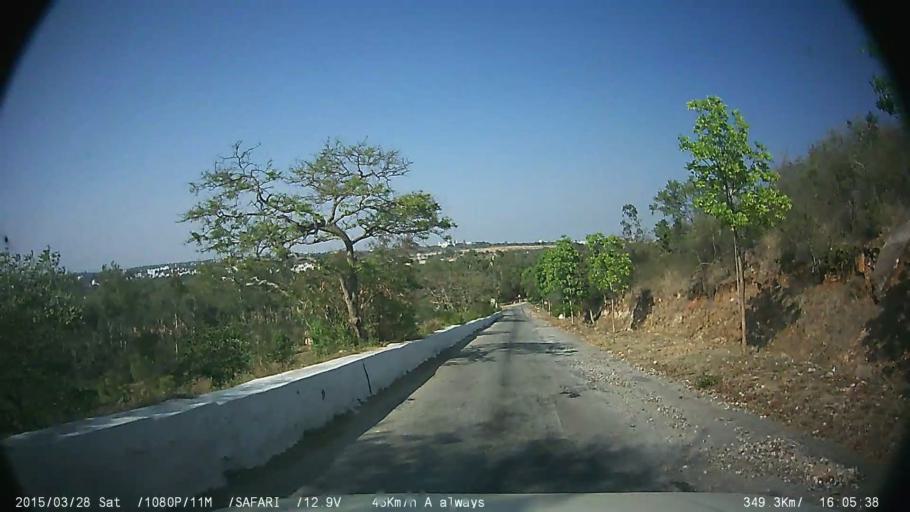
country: IN
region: Karnataka
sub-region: Mysore
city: Mysore
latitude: 12.2864
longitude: 76.6811
